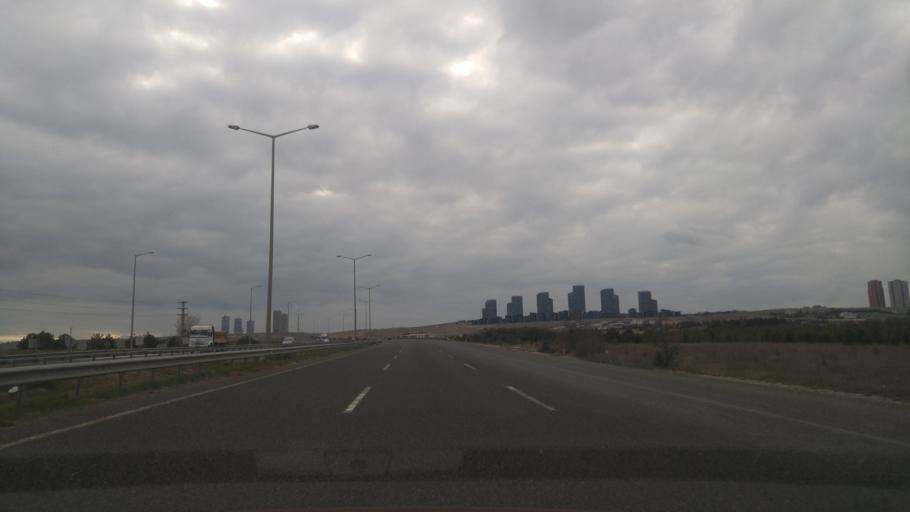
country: TR
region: Ankara
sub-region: Goelbasi
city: Golbasi
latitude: 39.7881
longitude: 32.7344
